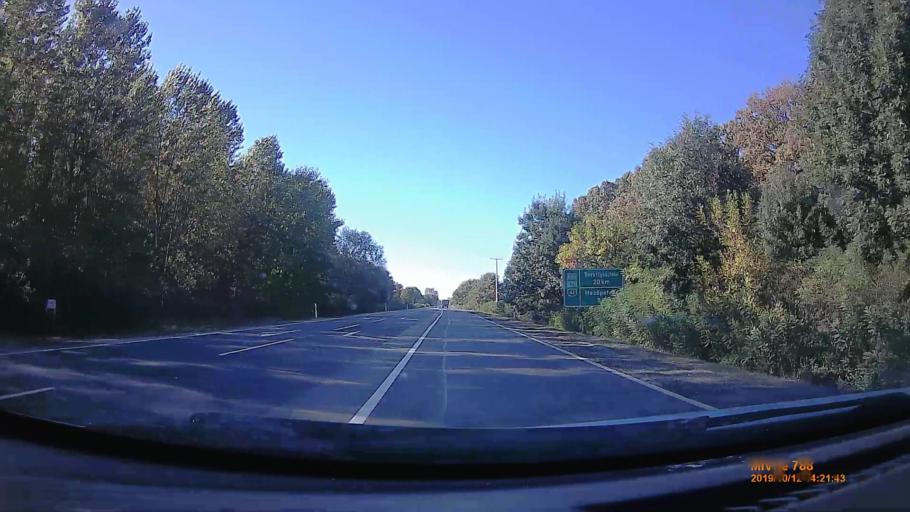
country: HU
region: Hajdu-Bihar
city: Biharkeresztes
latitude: 47.1401
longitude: 21.7285
